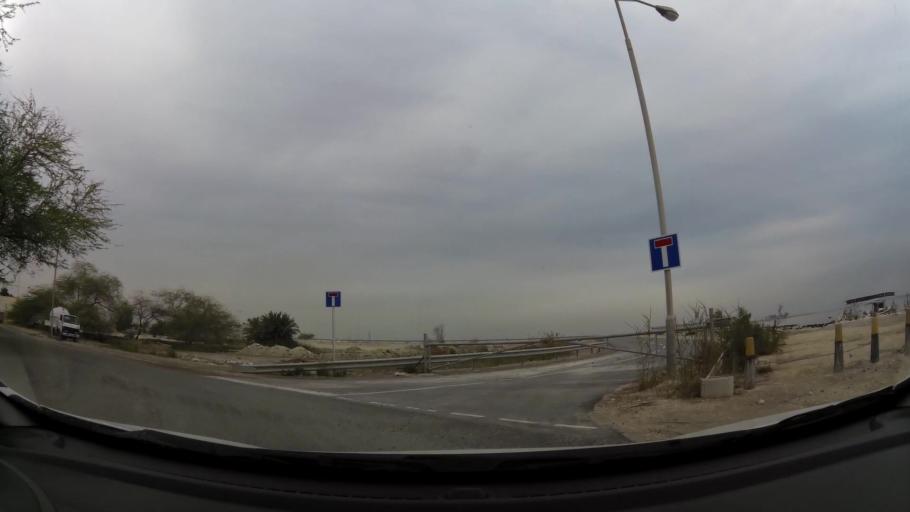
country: BH
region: Northern
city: Ar Rifa'
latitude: 26.0606
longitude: 50.6183
